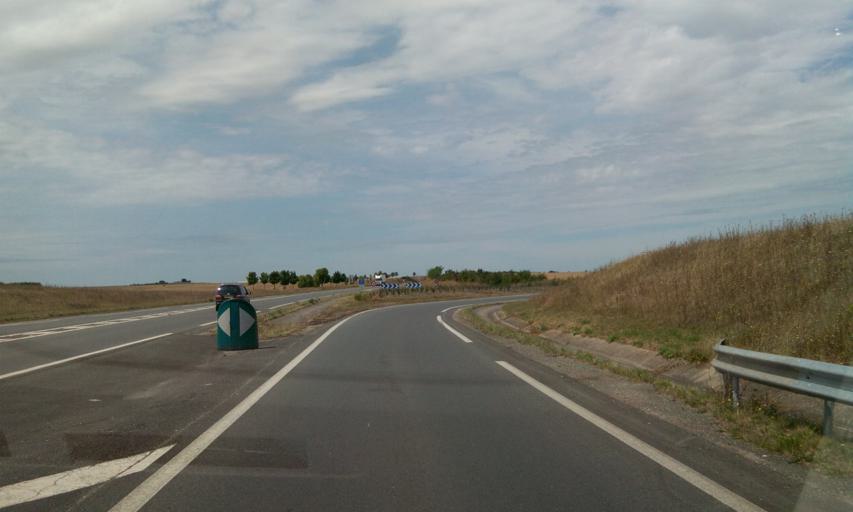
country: FR
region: Poitou-Charentes
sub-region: Departement des Deux-Sevres
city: Vouille
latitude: 46.3088
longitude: -0.3738
